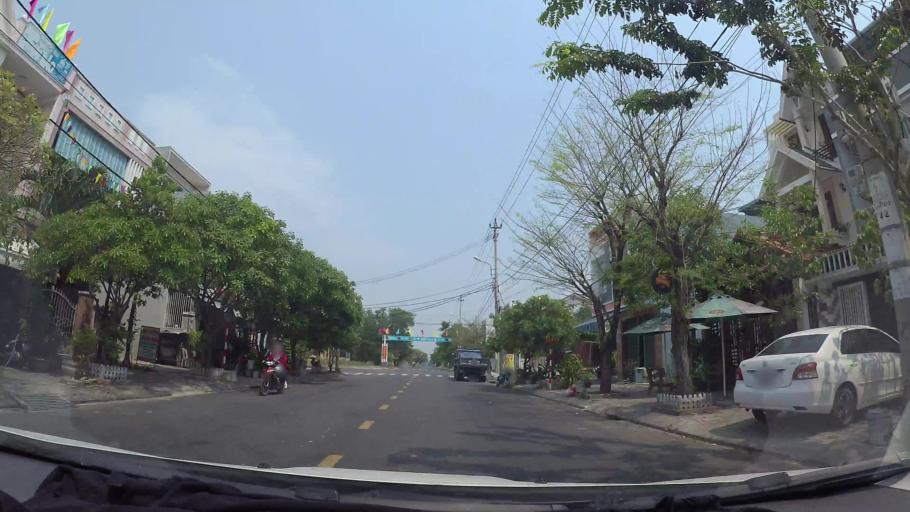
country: VN
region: Da Nang
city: Cam Le
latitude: 15.9879
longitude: 108.2138
